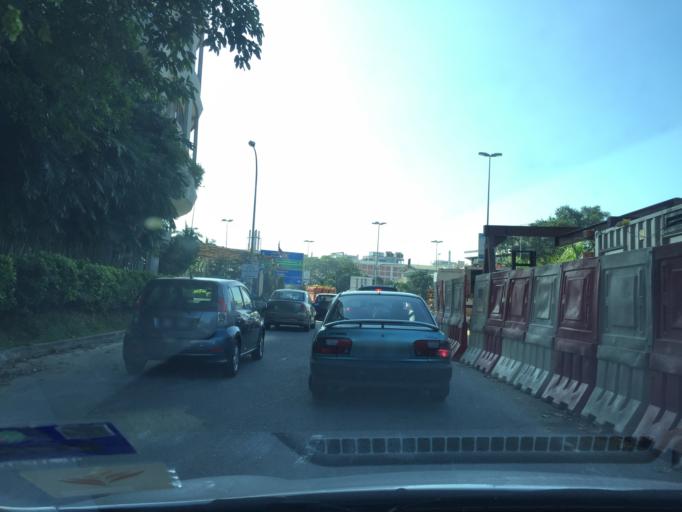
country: MY
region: Selangor
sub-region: Petaling
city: Petaling Jaya
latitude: 3.1180
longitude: 101.6294
